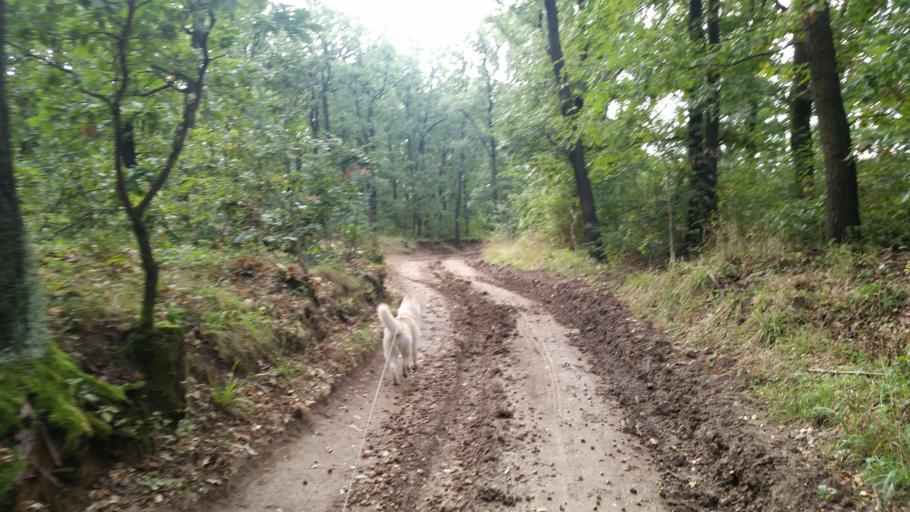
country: HU
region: Pest
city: Telki
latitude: 47.5626
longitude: 18.8247
